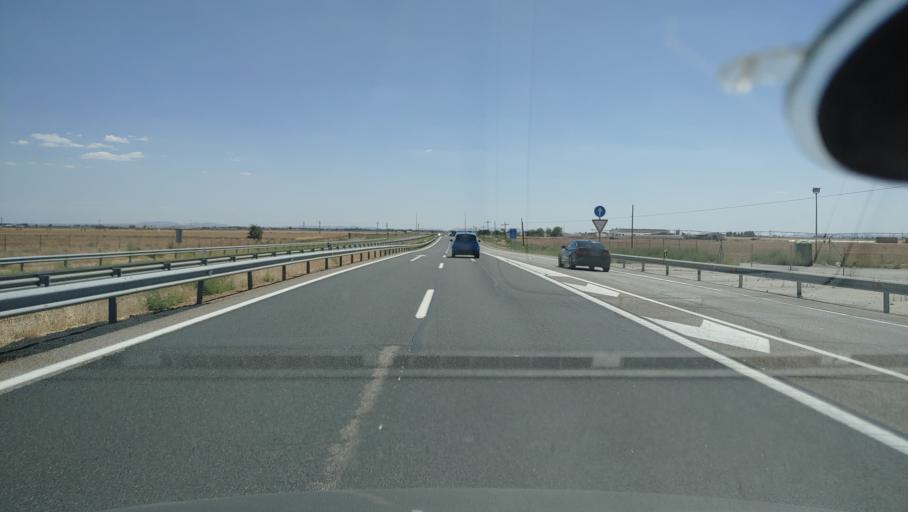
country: ES
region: Castille-La Mancha
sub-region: Provincia de Ciudad Real
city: Villarta de San Juan
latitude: 39.1636
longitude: -3.3918
